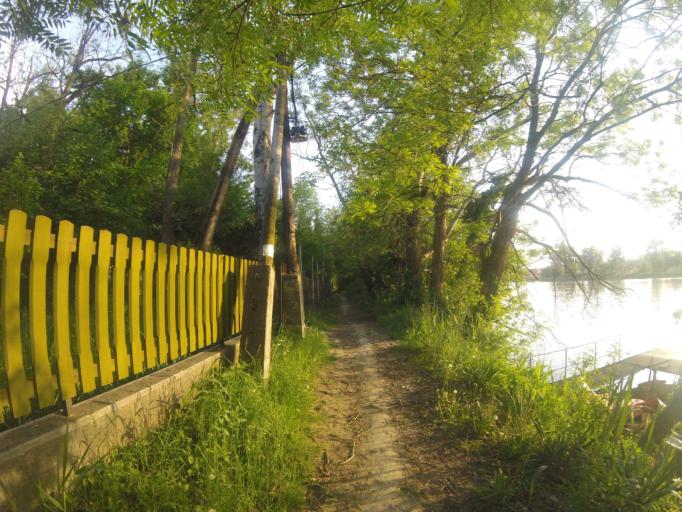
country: HU
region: Pest
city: Rackeve
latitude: 47.1910
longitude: 18.9525
